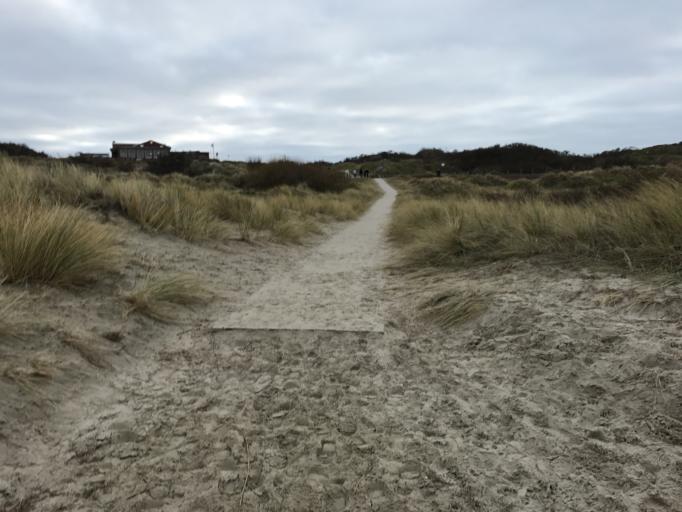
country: DE
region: Lower Saxony
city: Borkum
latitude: 53.6004
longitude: 6.6725
